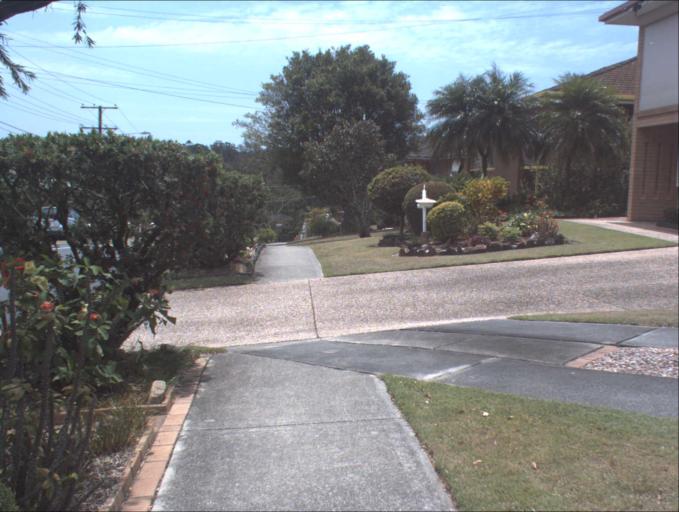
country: AU
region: Queensland
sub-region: Logan
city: Springwood
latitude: -27.6237
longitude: 153.1342
